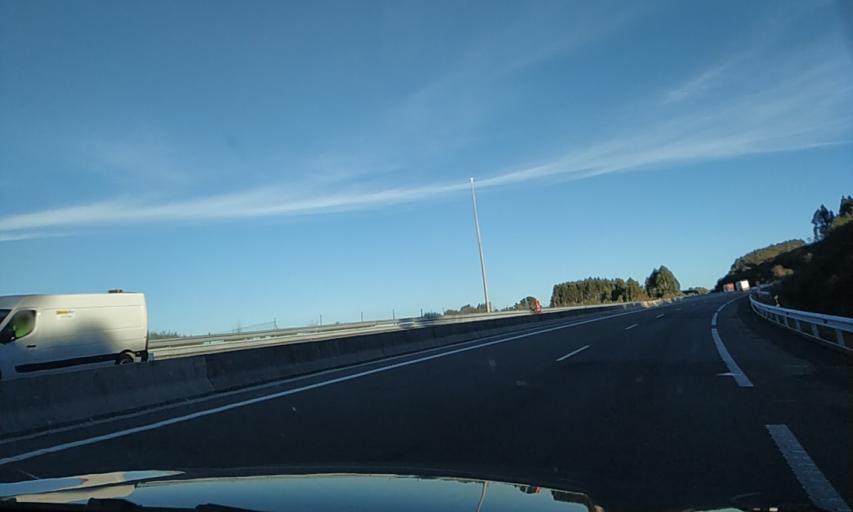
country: ES
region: Galicia
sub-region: Provincia de Pontevedra
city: Dozon
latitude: 42.5652
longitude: -8.0456
